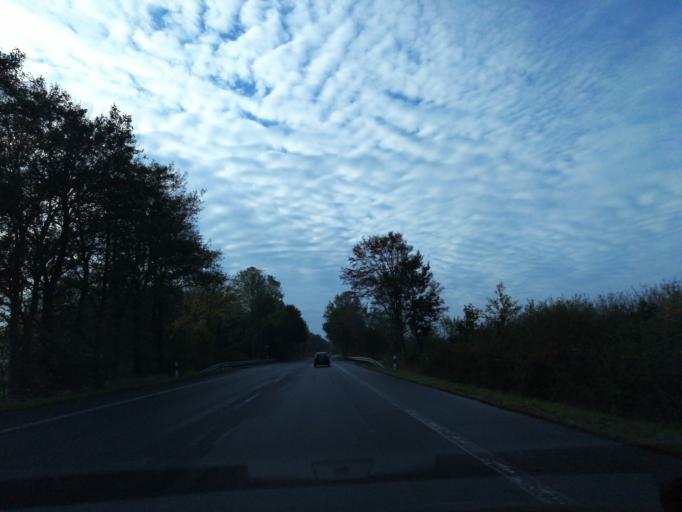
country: DE
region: Lower Saxony
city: Fedderwarden
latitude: 53.5668
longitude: 8.0549
